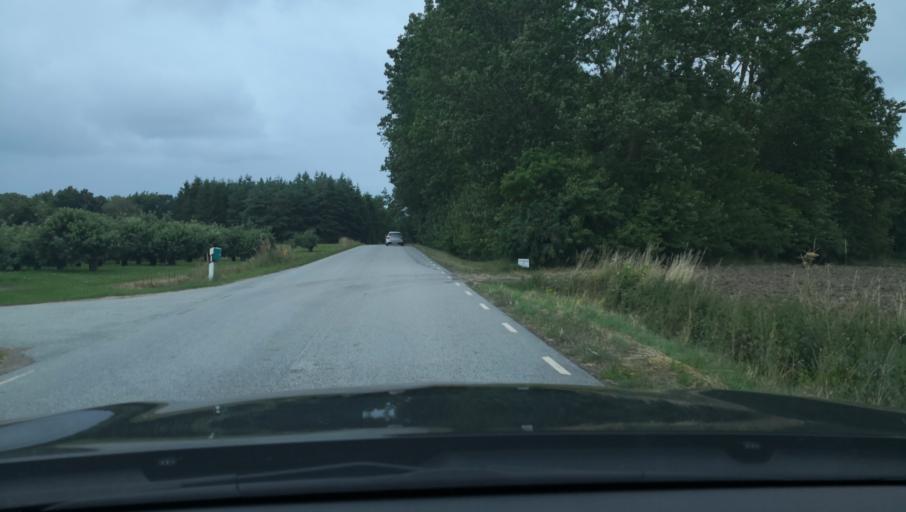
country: SE
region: Skane
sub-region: Simrishamns Kommun
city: Kivik
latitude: 55.6706
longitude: 14.2173
